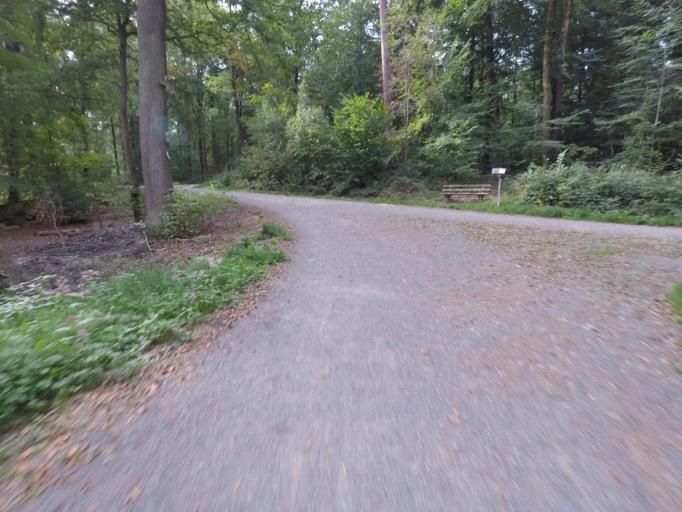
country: DE
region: Baden-Wuerttemberg
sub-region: Regierungsbezirk Stuttgart
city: Steinenbronn
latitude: 48.7239
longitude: 9.0909
